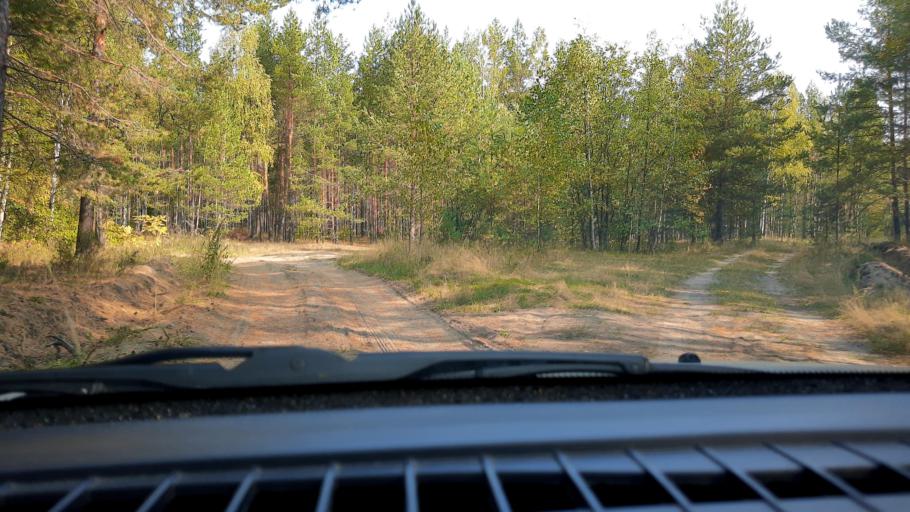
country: RU
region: Nizjnij Novgorod
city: Lukino
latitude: 56.3920
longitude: 43.6282
